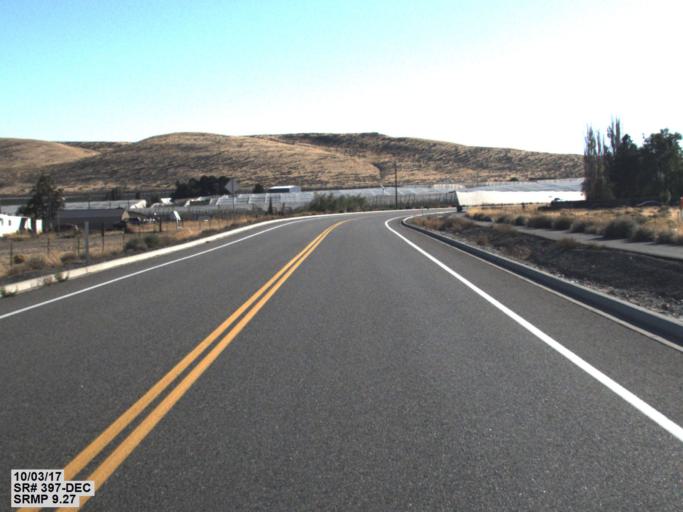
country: US
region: Washington
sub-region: Benton County
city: Finley
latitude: 46.1336
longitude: -119.0351
